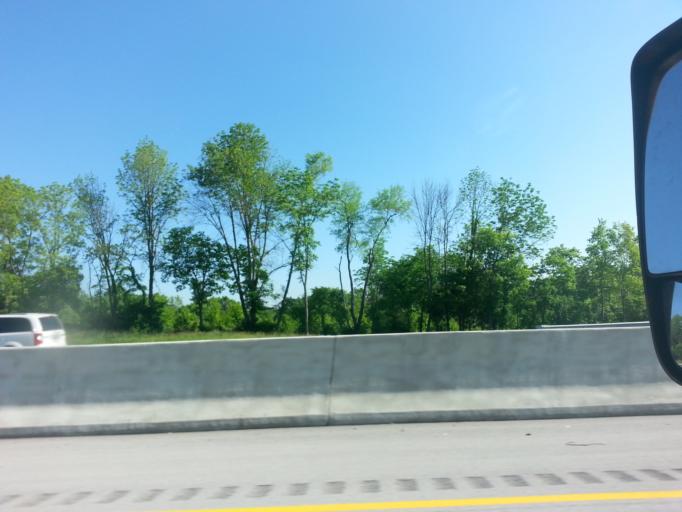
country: US
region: Kentucky
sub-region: Shelby County
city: Simpsonville
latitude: 38.2171
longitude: -85.4070
